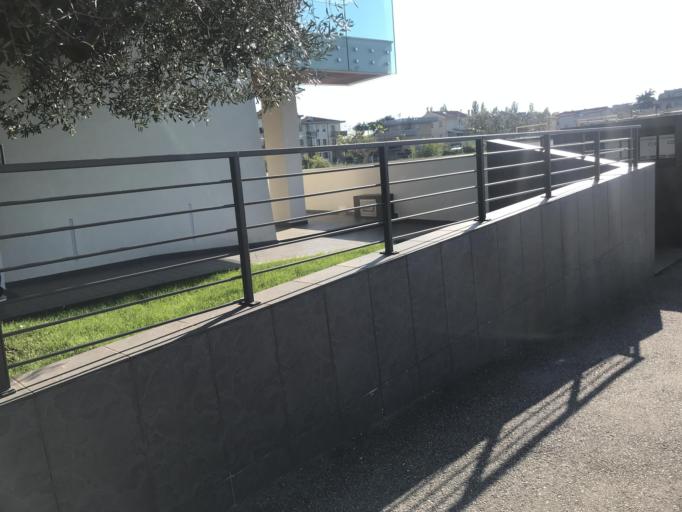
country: IT
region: Emilia-Romagna
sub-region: Provincia di Rimini
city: Rimini
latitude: 44.0474
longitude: 12.5735
